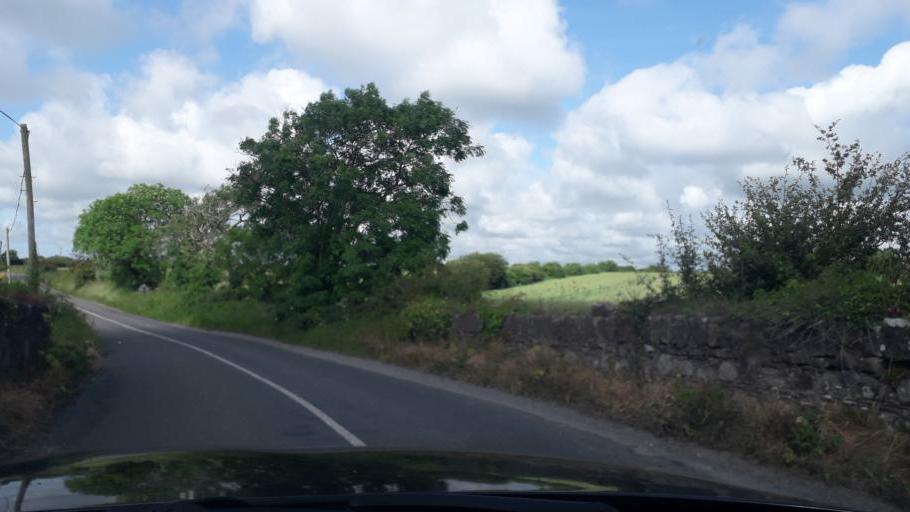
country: IE
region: Leinster
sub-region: Loch Garman
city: Loch Garman
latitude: 52.2669
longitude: -6.5544
